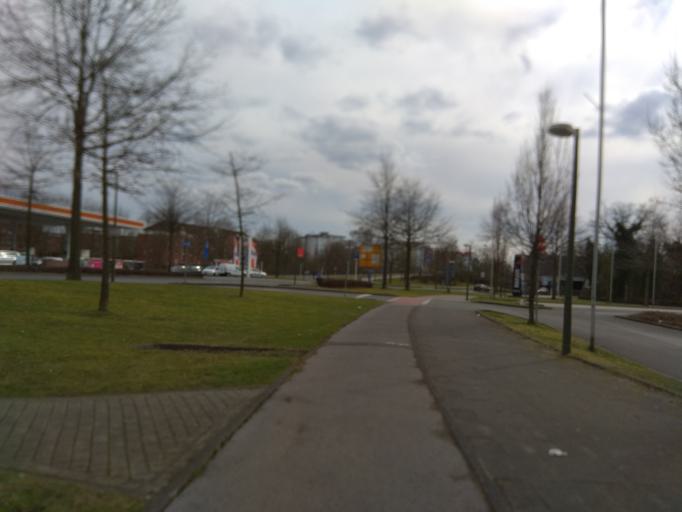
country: DE
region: North Rhine-Westphalia
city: Marl
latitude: 51.6564
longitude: 7.1006
